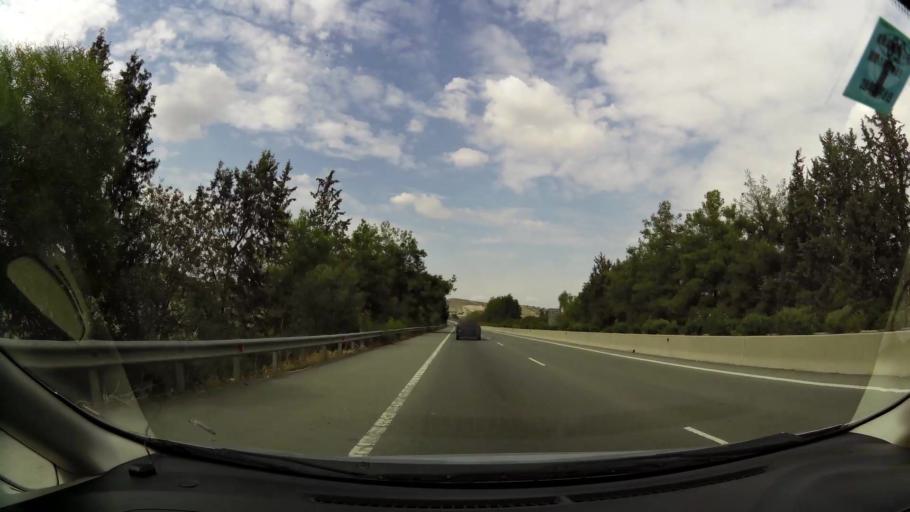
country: CY
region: Lefkosia
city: Lympia
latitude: 34.9957
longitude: 33.4417
